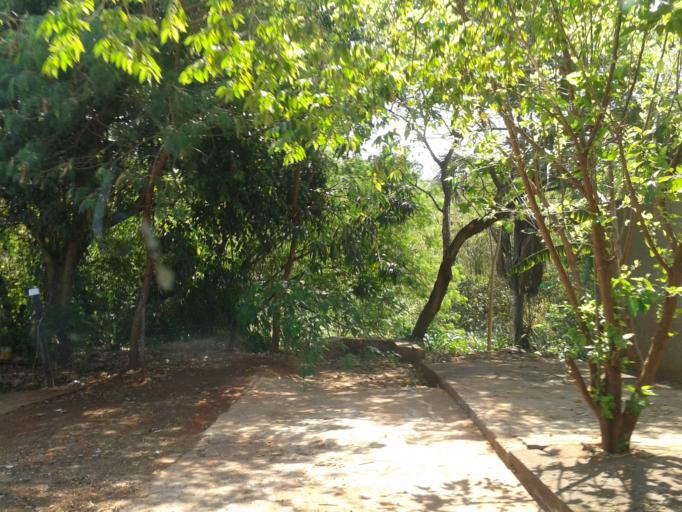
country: BR
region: Minas Gerais
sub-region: Ituiutaba
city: Ituiutaba
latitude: -18.9691
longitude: -49.4867
